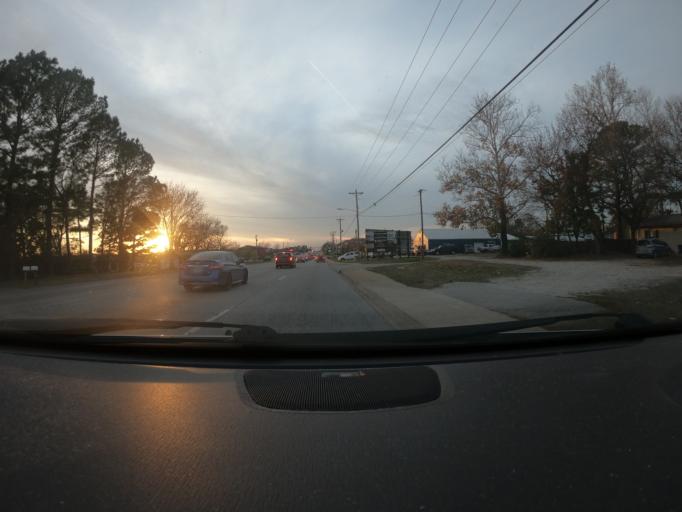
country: US
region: Arkansas
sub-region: Benton County
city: Bentonville
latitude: 36.3353
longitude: -94.1950
